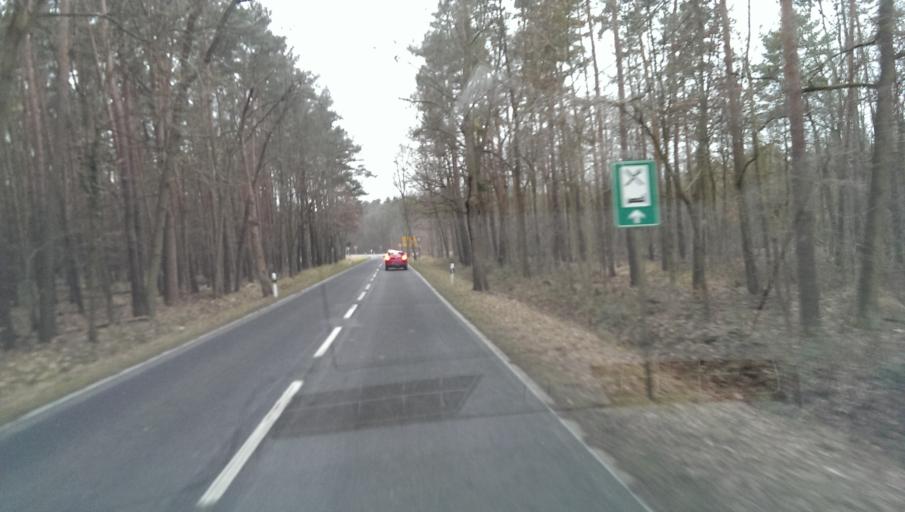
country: DE
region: Brandenburg
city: Ludwigsfelde
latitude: 52.2811
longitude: 13.2938
